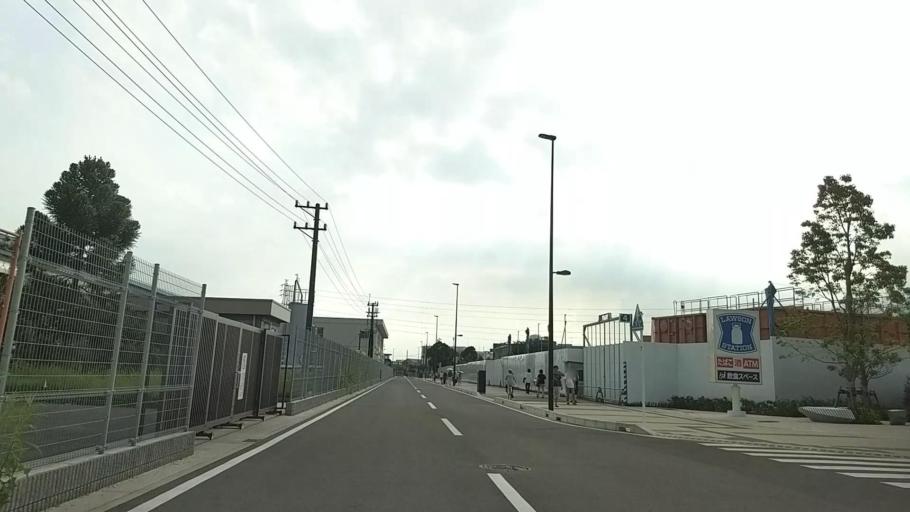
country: JP
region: Kanagawa
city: Atsugi
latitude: 35.4528
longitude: 139.3895
